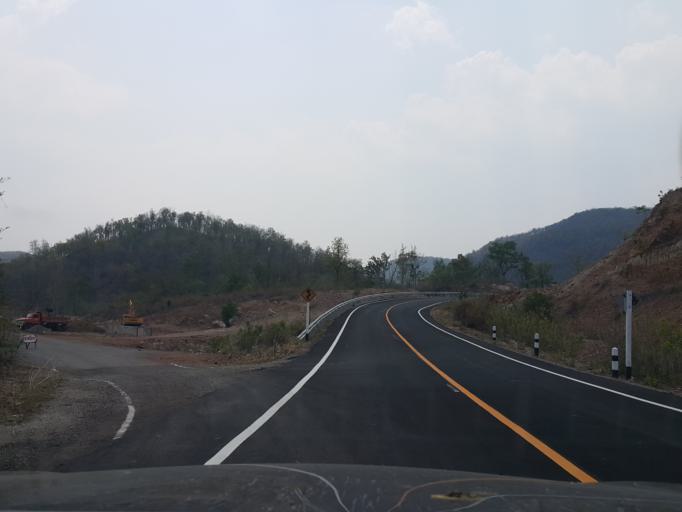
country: TH
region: Lampang
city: Mae Phrik
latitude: 17.5036
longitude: 99.0782
